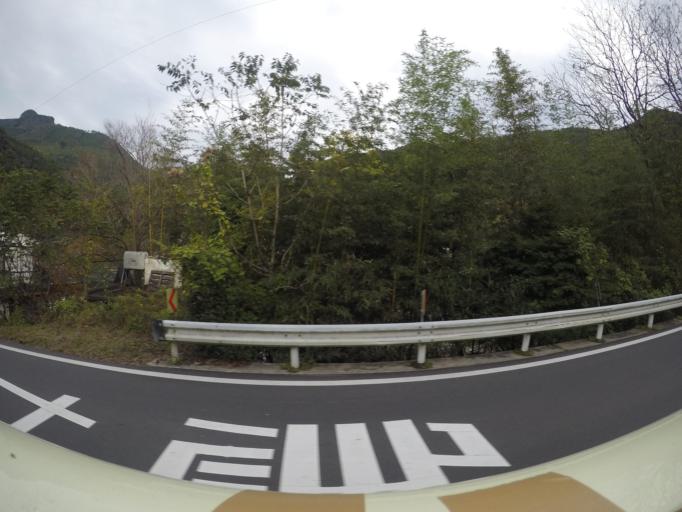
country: JP
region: Gunma
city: Yoshii
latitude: 36.1226
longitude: 138.9410
